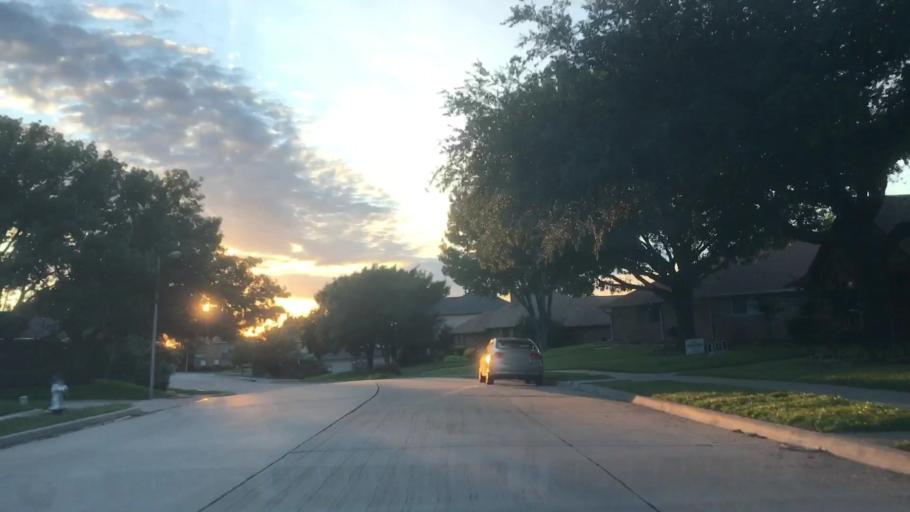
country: US
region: Texas
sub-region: Dallas County
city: Carrollton
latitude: 32.9756
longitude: -96.8794
